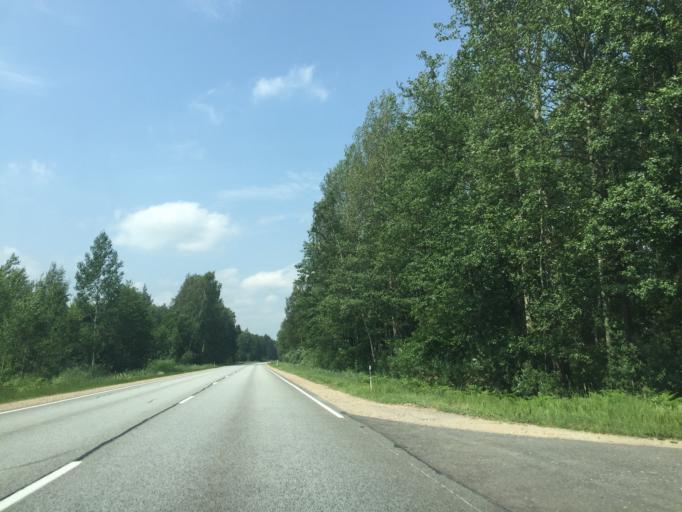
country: LV
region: Kekava
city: Balozi
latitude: 56.8241
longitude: 24.0713
